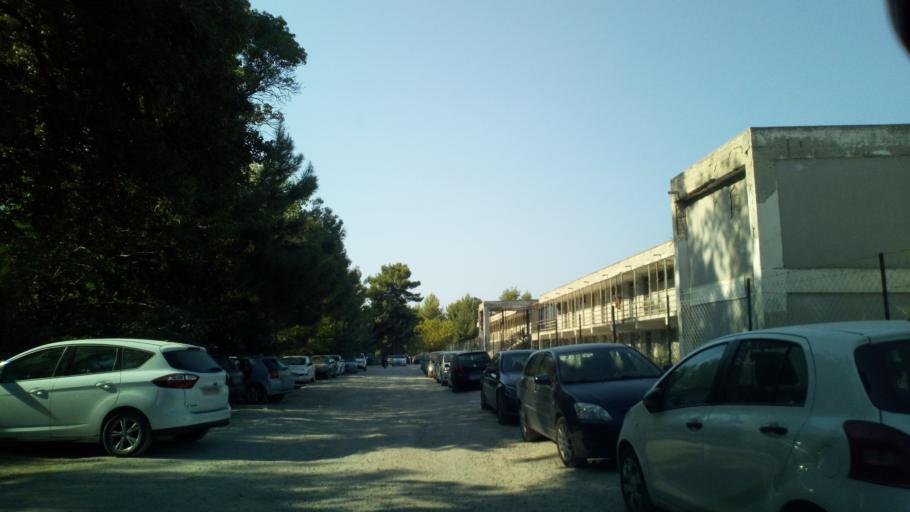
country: GR
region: Central Macedonia
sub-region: Nomos Chalkidikis
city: Pefkochori
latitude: 39.9603
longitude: 23.6757
